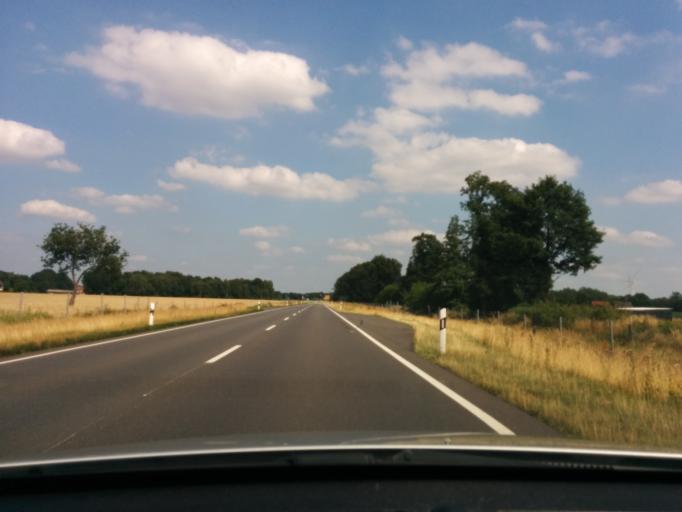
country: DE
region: North Rhine-Westphalia
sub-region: Regierungsbezirk Munster
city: Wettringen
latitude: 52.1990
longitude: 7.3162
